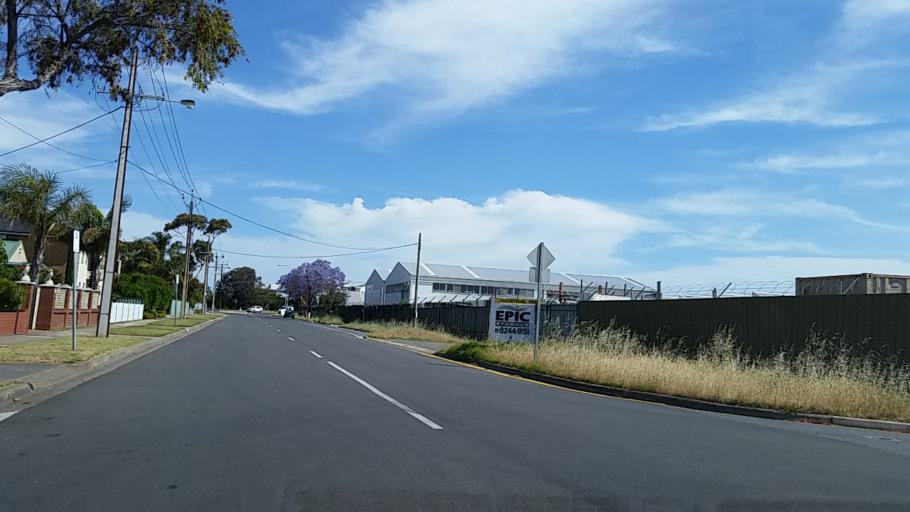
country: AU
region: South Australia
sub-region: Charles Sturt
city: Albert Park
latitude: -34.8811
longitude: 138.5216
